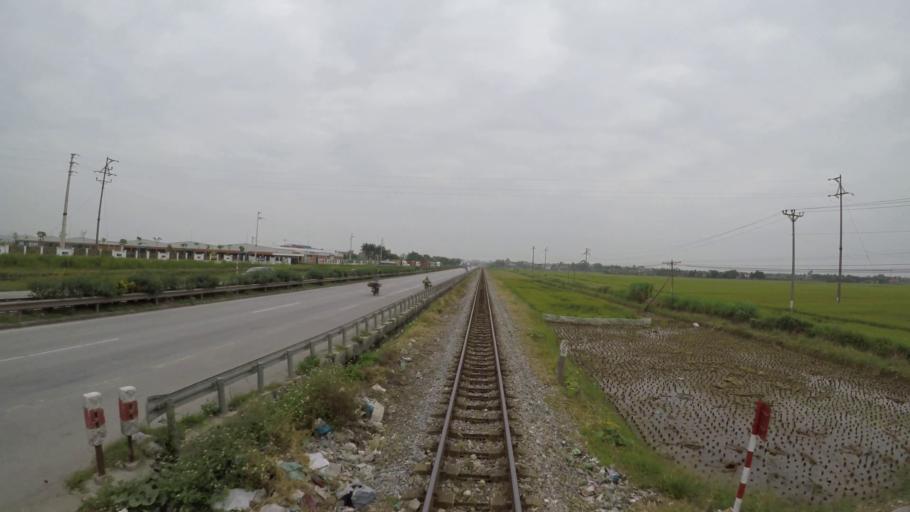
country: VN
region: Hai Duong
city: Phu Thai
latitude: 20.9625
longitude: 106.5185
